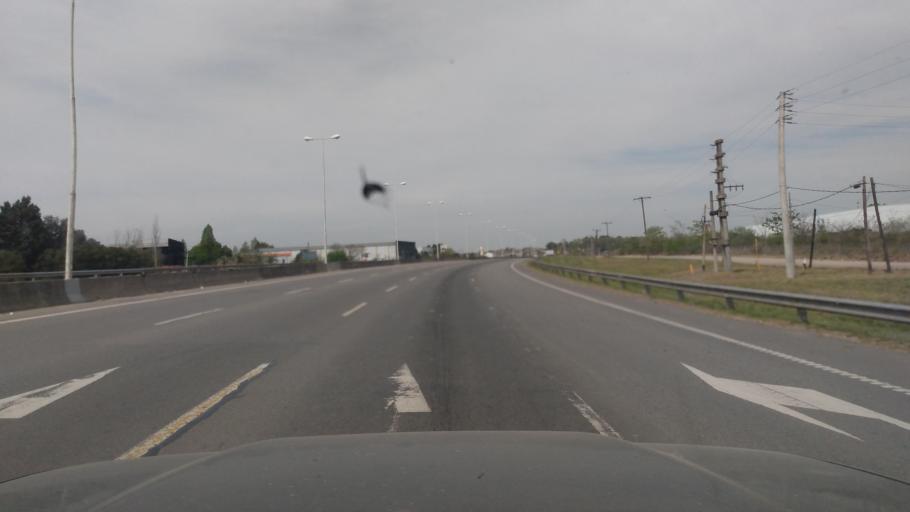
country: AR
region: Buenos Aires
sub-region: Partido de Pilar
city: Pilar
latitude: -34.4126
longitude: -59.0046
